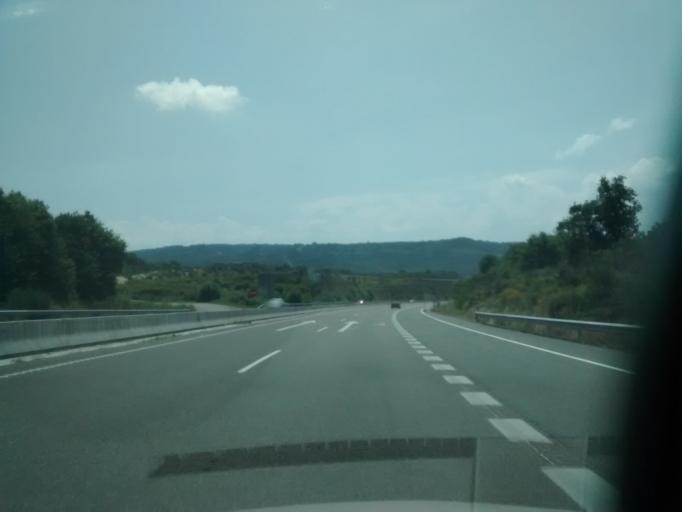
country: ES
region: Galicia
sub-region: Provincia de Ourense
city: Maside
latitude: 42.3977
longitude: -8.0008
